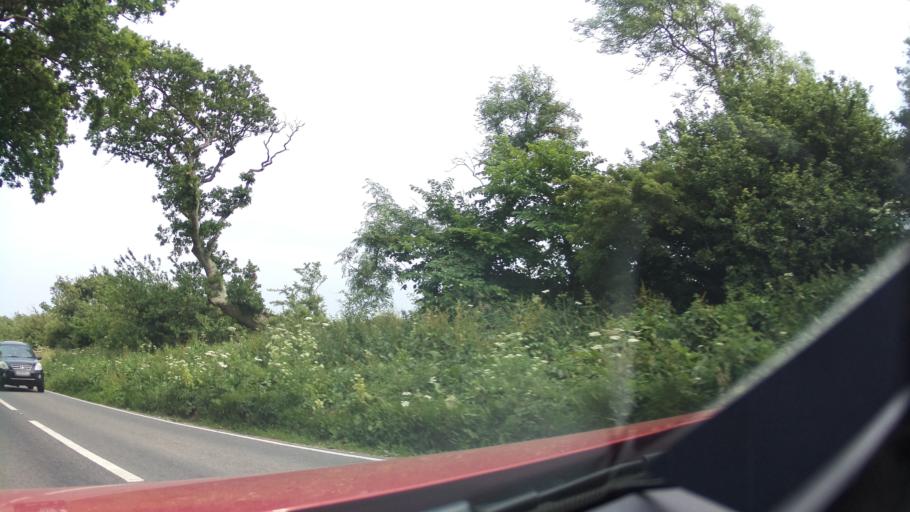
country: GB
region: England
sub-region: Devon
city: Colyton
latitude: 50.7247
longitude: -3.0251
